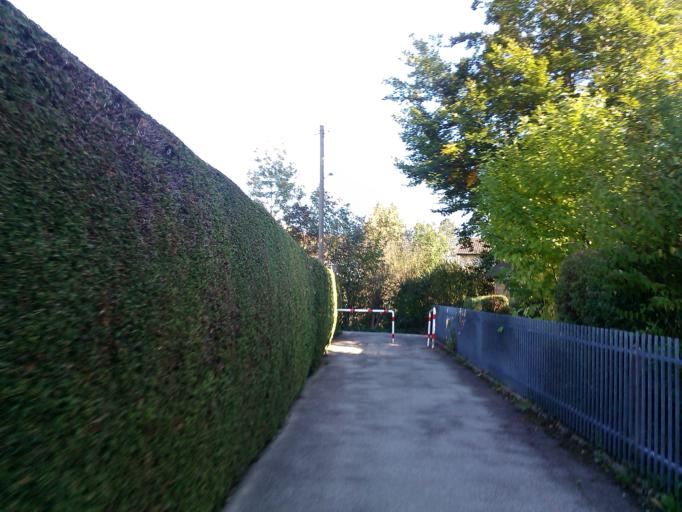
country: DE
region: Bavaria
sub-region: Upper Bavaria
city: Gauting
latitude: 48.0652
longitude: 11.3709
